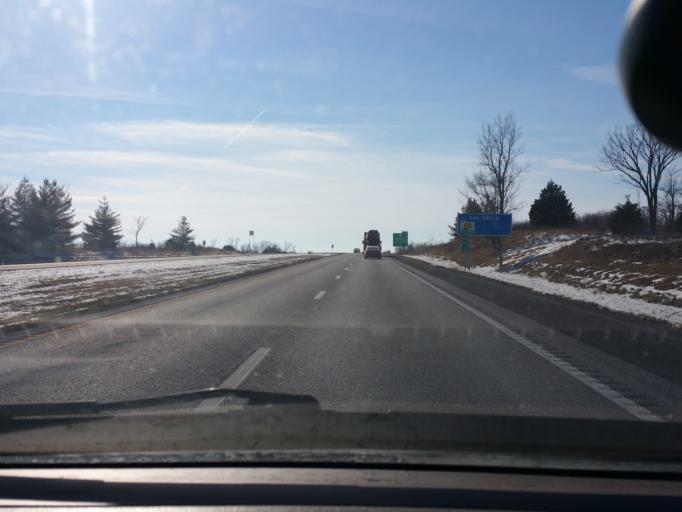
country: US
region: Missouri
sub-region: Clinton County
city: Cameron
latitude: 39.8610
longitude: -94.1736
